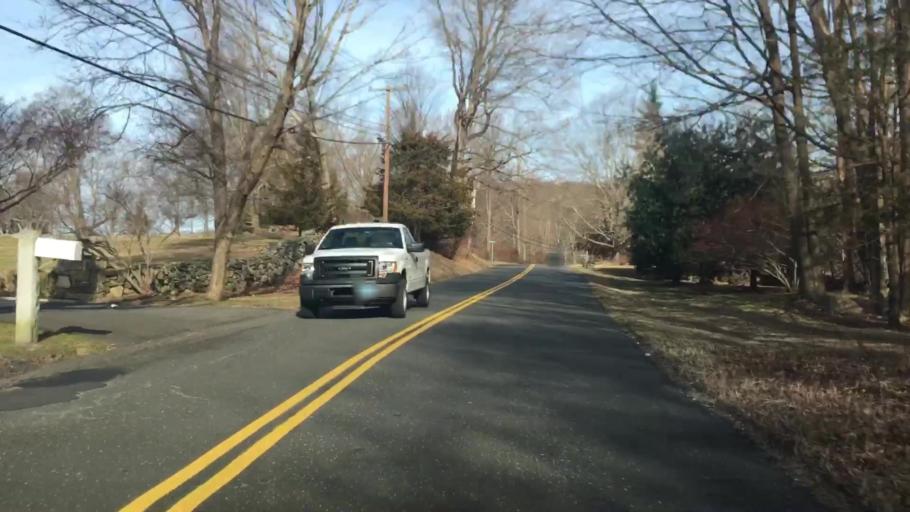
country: US
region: New York
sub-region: Putnam County
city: Peach Lake
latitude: 41.3719
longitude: -73.5275
